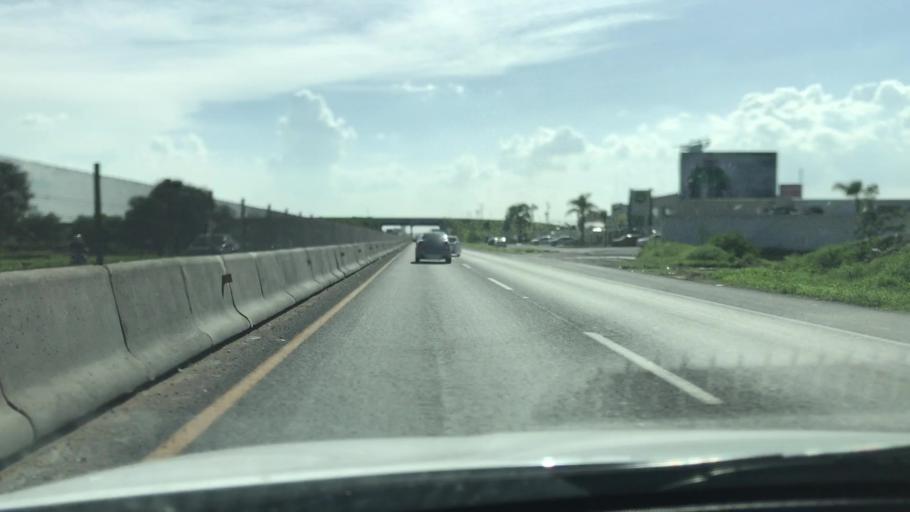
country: MX
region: Guanajuato
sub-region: Celaya
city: Colonia Pedro Maria Anaya
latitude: 20.5173
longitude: -100.8682
